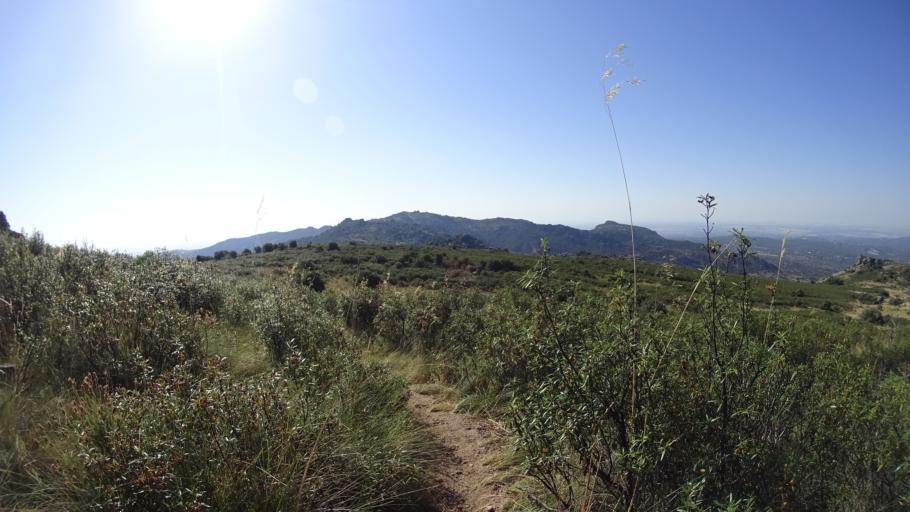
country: ES
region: Madrid
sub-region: Provincia de Madrid
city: Moralzarzal
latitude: 40.6502
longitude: -3.9435
